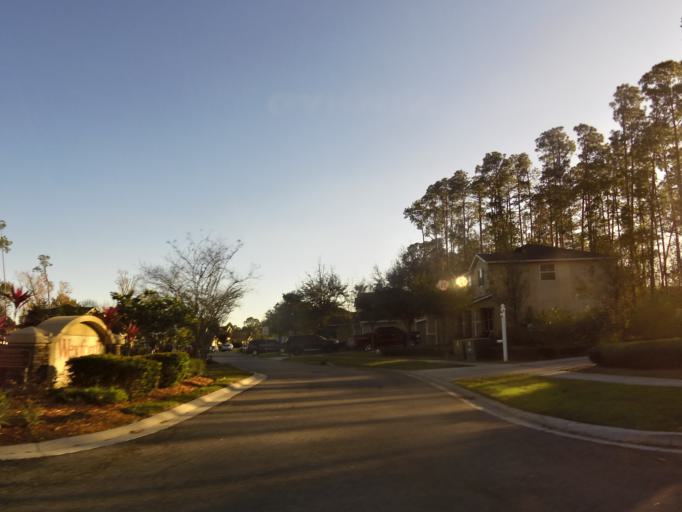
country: US
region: Florida
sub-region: Saint Johns County
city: Fruit Cove
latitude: 30.2059
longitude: -81.5873
